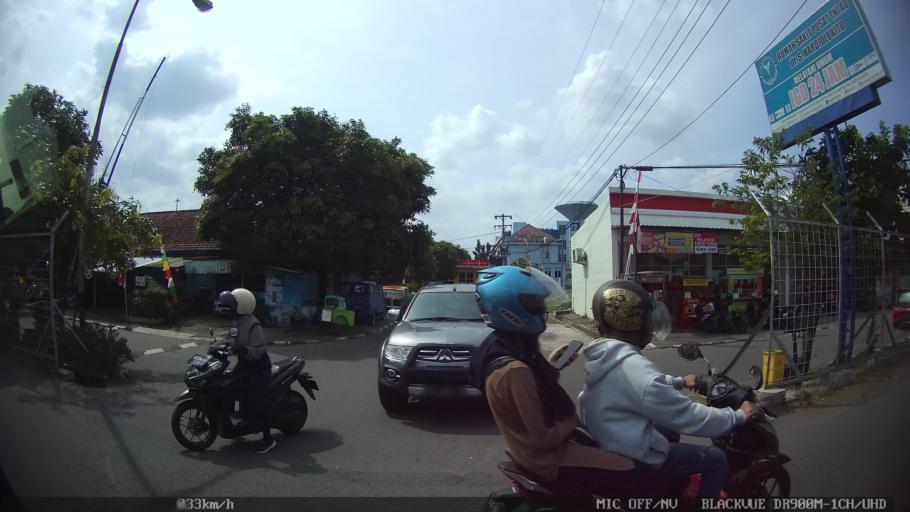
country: ID
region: Daerah Istimewa Yogyakarta
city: Depok
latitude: -7.7986
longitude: 110.4125
